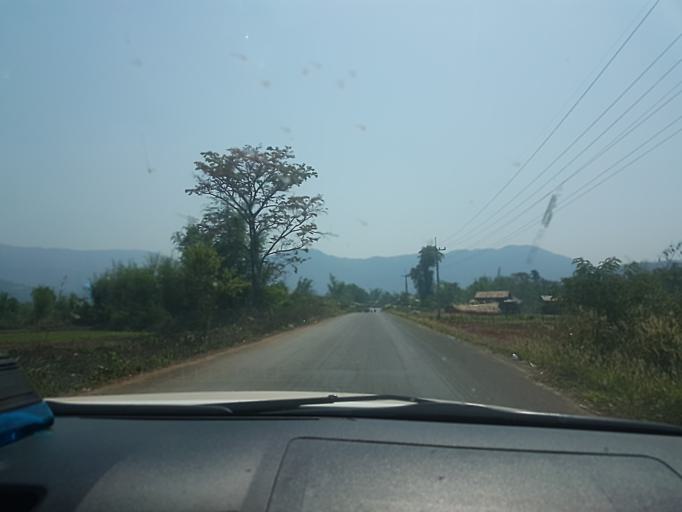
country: LA
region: Bolikhamxai
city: Ban Nahin
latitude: 18.5331
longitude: 104.4775
